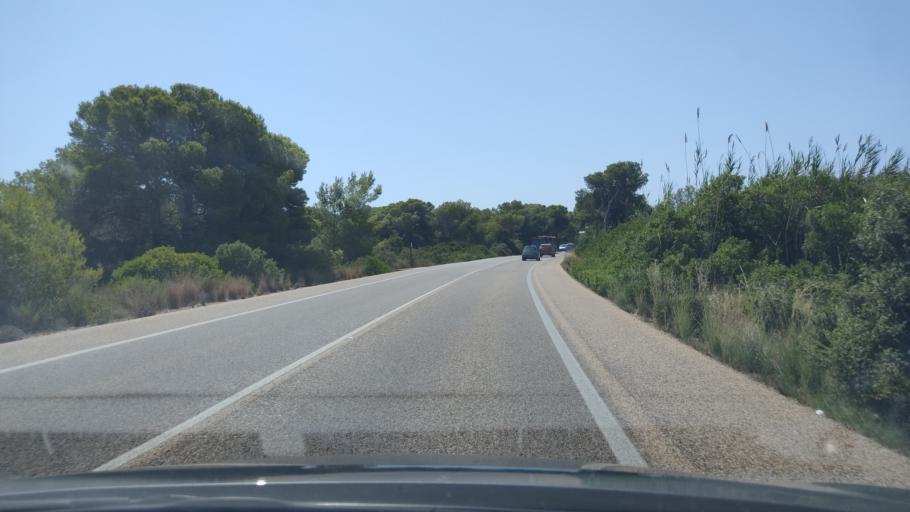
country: ES
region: Valencia
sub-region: Provincia de Valencia
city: Sollana
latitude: 39.3307
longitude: -0.3122
